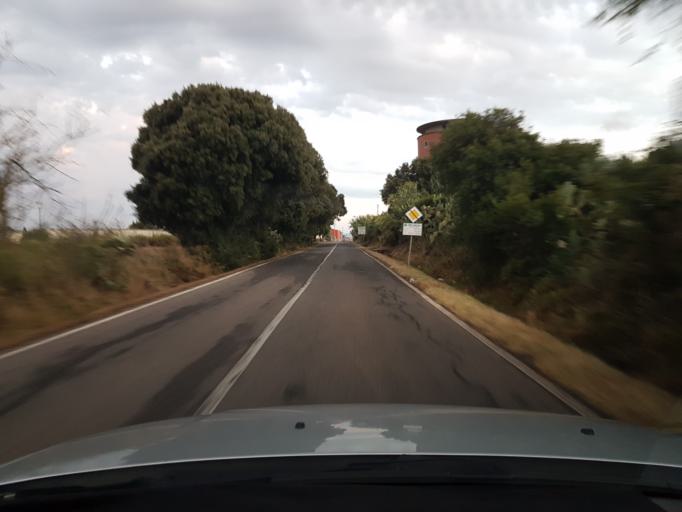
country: IT
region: Sardinia
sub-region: Provincia di Oristano
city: Tramatza
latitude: 40.0075
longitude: 8.6469
